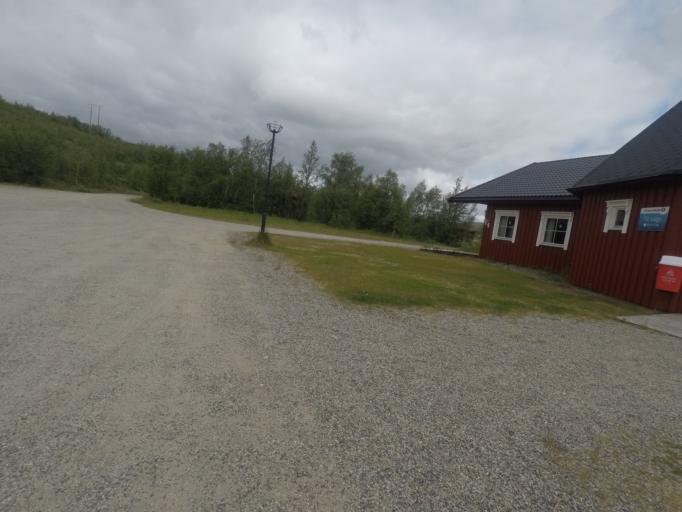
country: NO
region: Finnmark Fylke
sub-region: Alta
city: Alta
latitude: 69.4261
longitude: 23.6207
